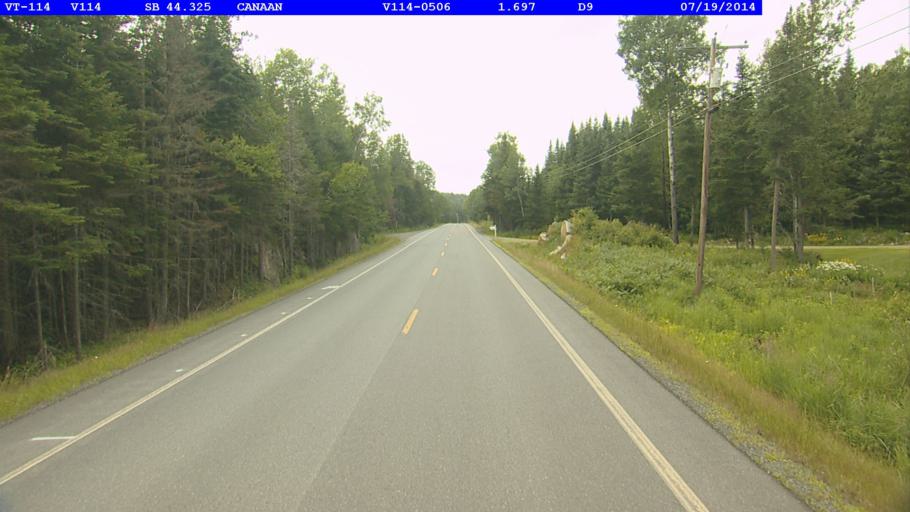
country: CA
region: Quebec
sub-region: Estrie
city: Coaticook
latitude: 45.0058
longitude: -71.6594
